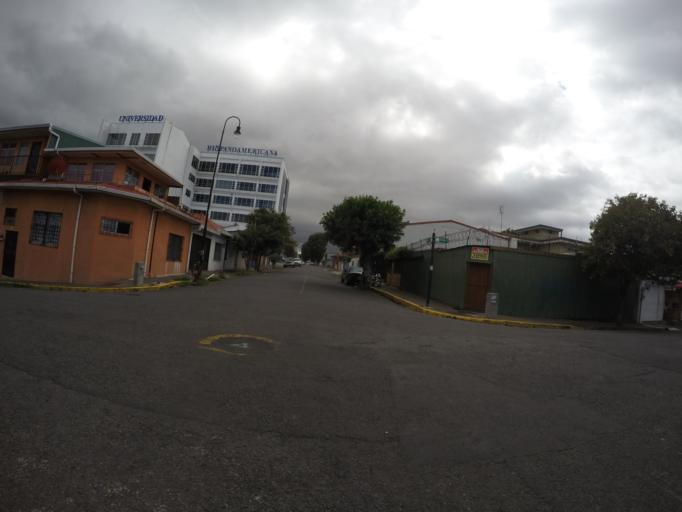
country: CR
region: San Jose
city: Calle Blancos
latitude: 9.9396
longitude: -84.0667
